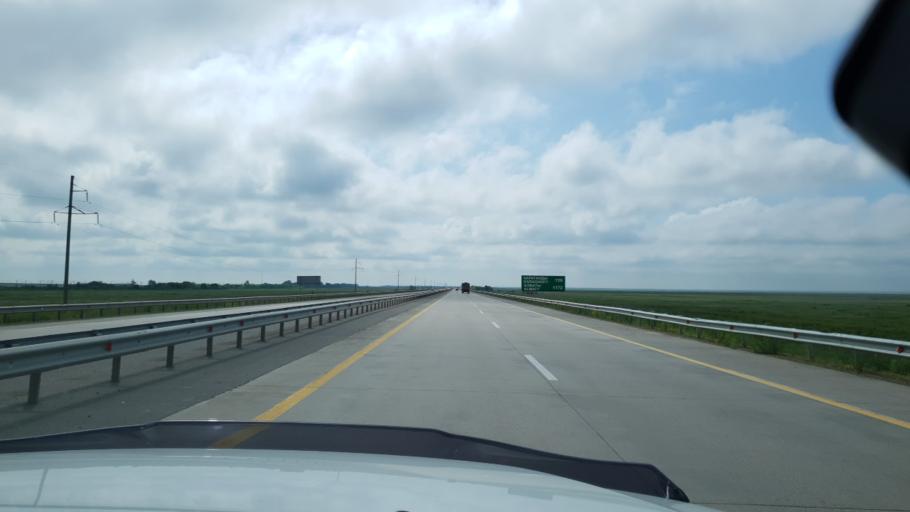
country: KZ
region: Astana Qalasy
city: Astana
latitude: 50.9926
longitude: 71.9061
